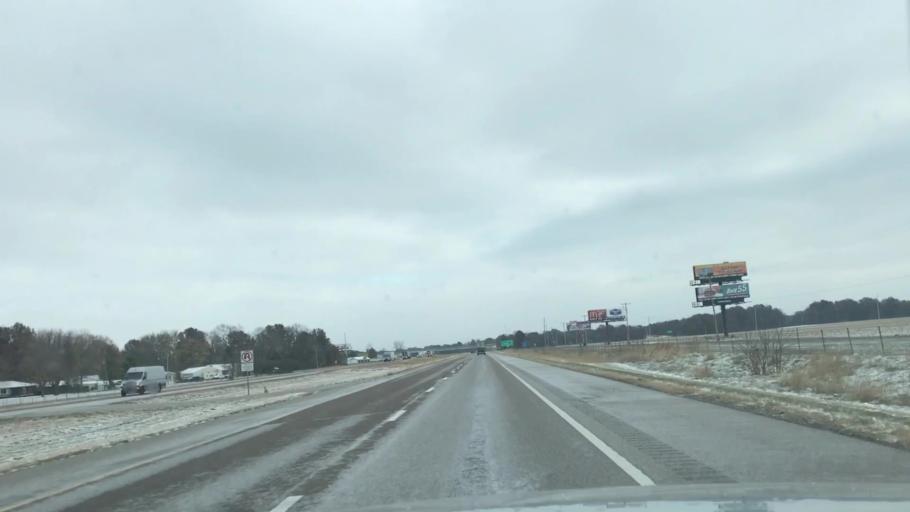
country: US
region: Illinois
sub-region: Macoupin County
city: Staunton
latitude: 38.9612
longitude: -89.7616
